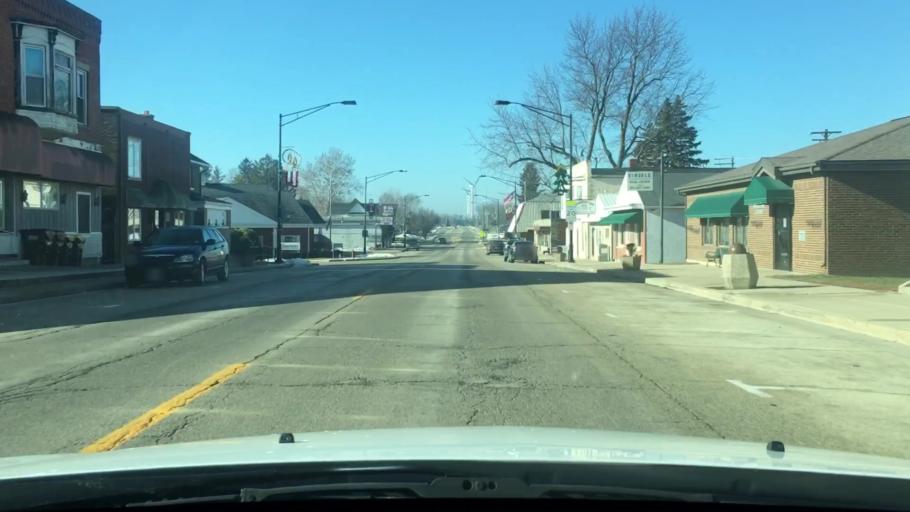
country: US
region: Illinois
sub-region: DeKalb County
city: Waterman
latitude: 41.7680
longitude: -88.8729
